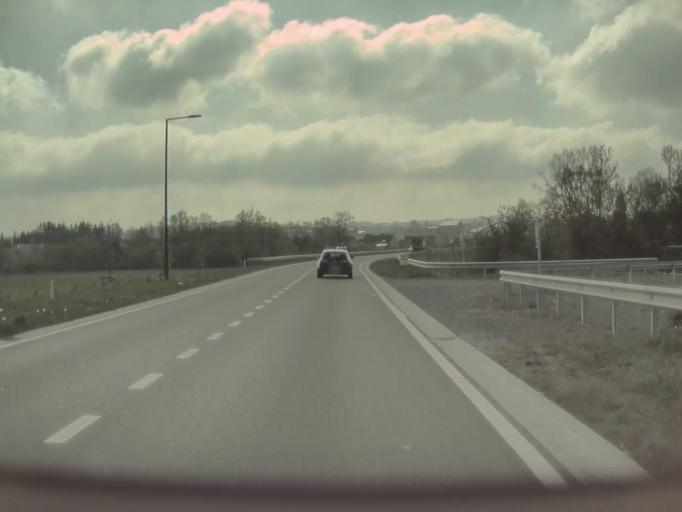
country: BE
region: Wallonia
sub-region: Province du Luxembourg
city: Marche-en-Famenne
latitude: 50.2322
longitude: 5.3094
